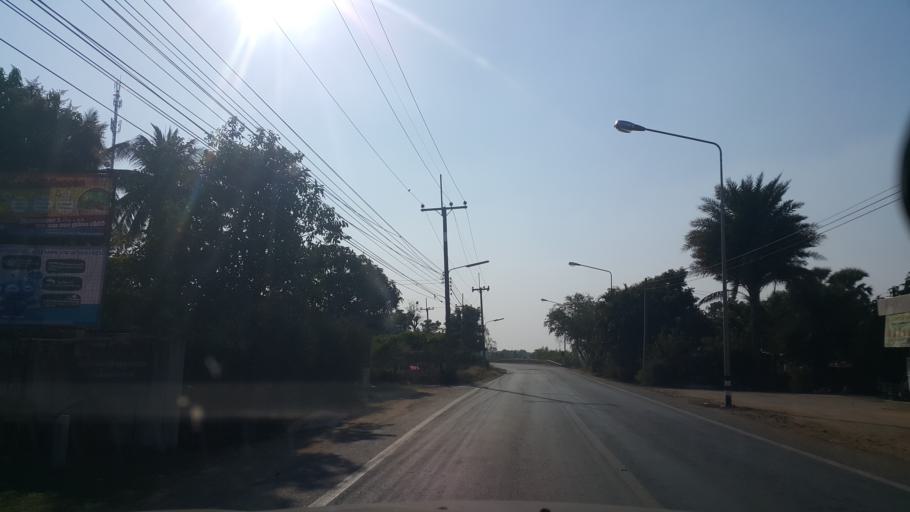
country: TH
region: Nakhon Ratchasima
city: Phimai
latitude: 15.1816
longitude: 102.4113
